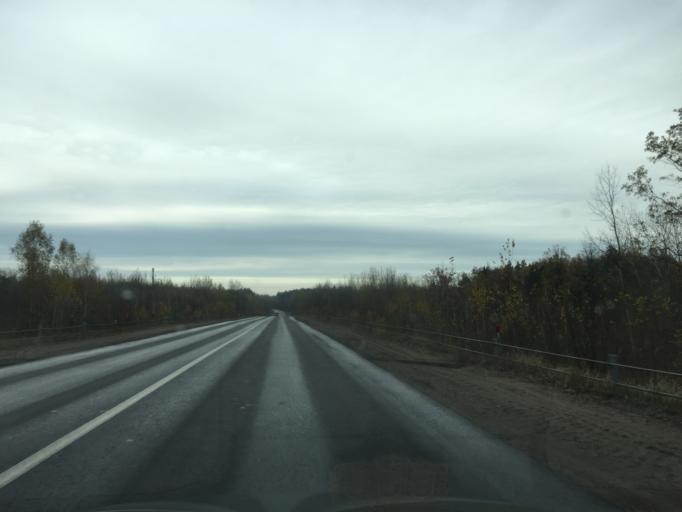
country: BY
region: Gomel
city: Gomel
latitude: 52.4179
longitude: 30.8286
